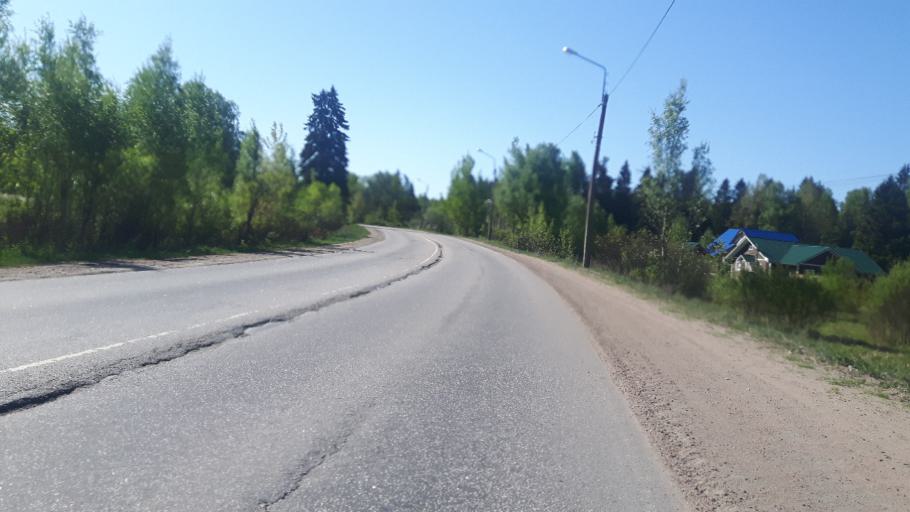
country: RU
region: Leningrad
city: Vyborg
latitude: 60.6531
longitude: 28.7444
